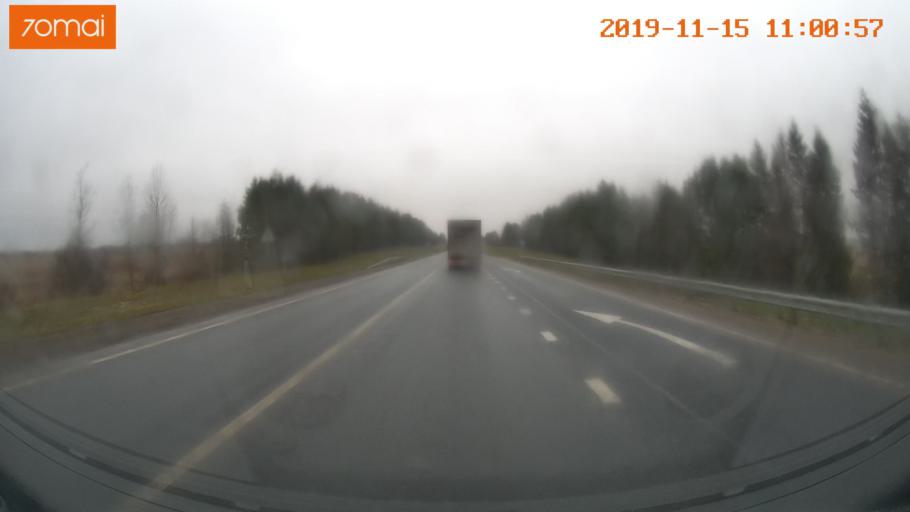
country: RU
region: Vologda
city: Chebsara
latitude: 59.1349
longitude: 38.9106
